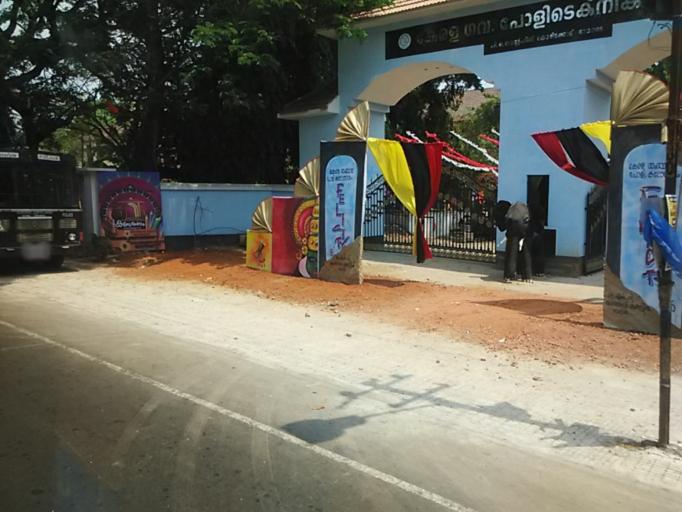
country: IN
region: Kerala
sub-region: Kozhikode
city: Kozhikode
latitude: 11.2860
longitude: 75.7680
